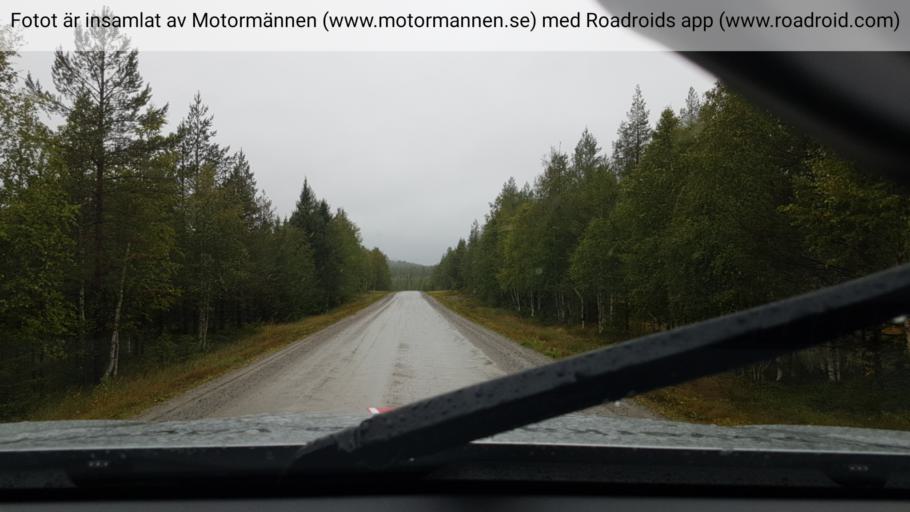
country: SE
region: Vaesterbotten
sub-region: Asele Kommun
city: Insjon
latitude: 64.0867
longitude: 17.9065
